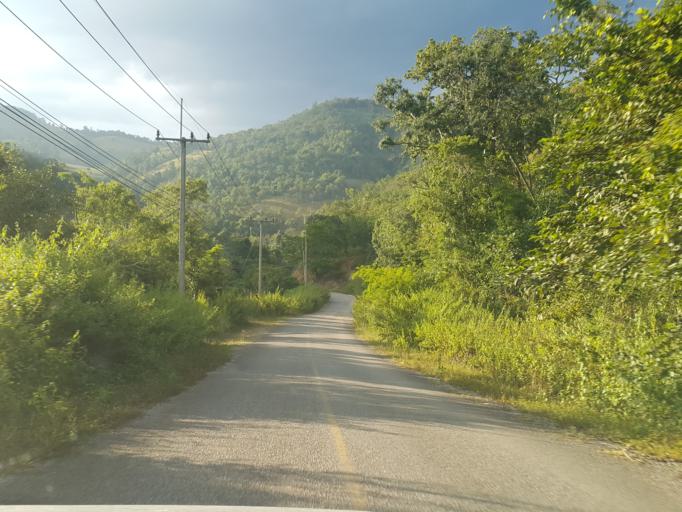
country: TH
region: Chiang Mai
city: Mae Chaem
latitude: 18.7369
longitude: 98.2289
